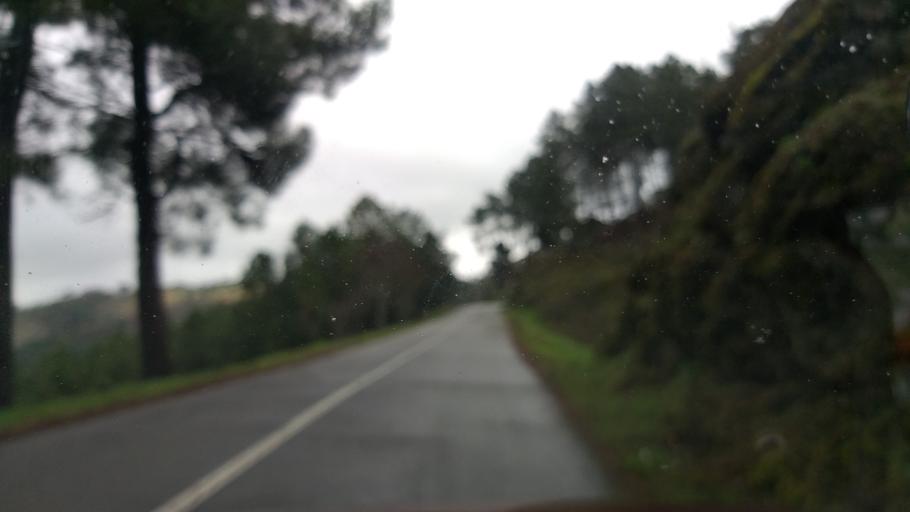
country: PT
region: Guarda
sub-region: Celorico da Beira
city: Celorico da Beira
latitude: 40.7080
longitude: -7.4272
